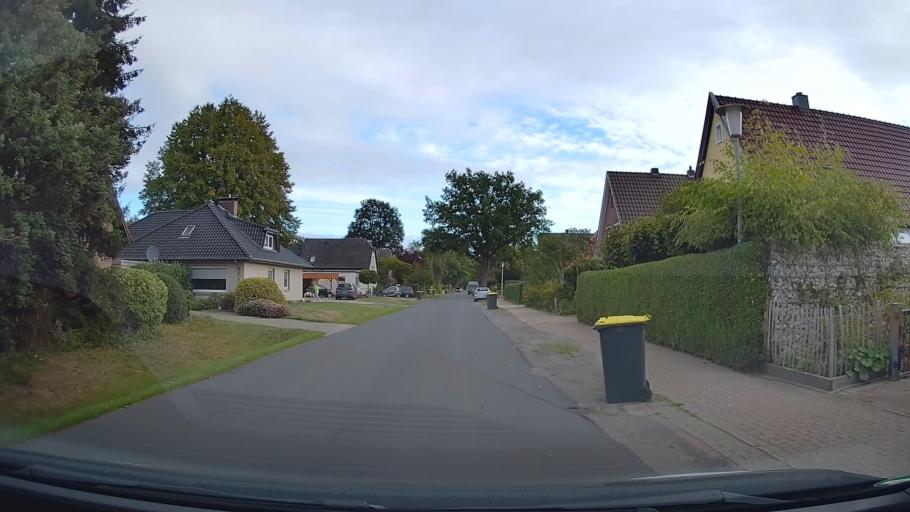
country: DE
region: Lower Saxony
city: Oldenburg
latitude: 53.1422
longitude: 8.1617
